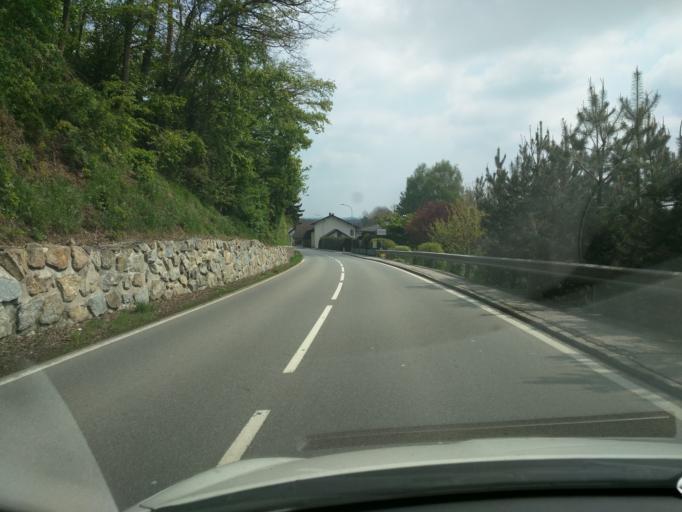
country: AT
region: Lower Austria
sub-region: Politischer Bezirk Melk
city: Blindenmarkt
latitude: 48.1265
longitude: 15.0001
